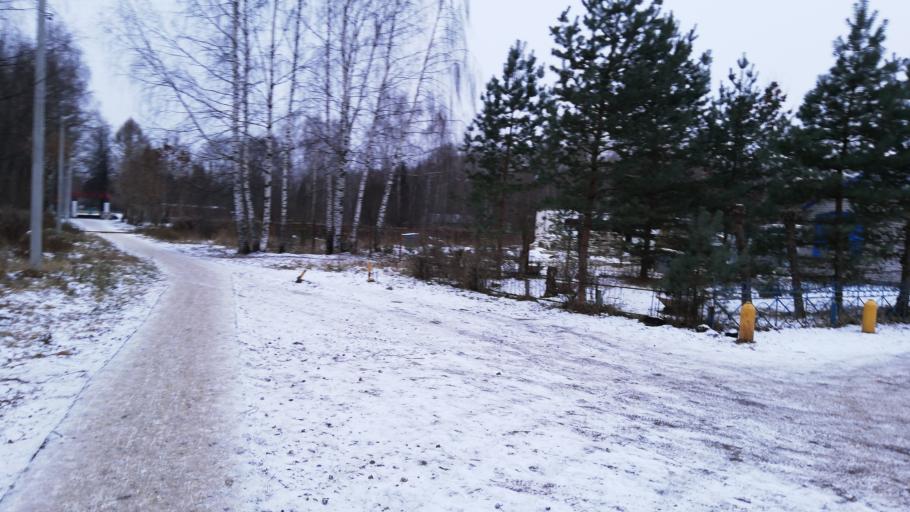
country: RU
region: Jaroslavl
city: Yaroslavl
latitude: 57.7252
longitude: 39.8186
